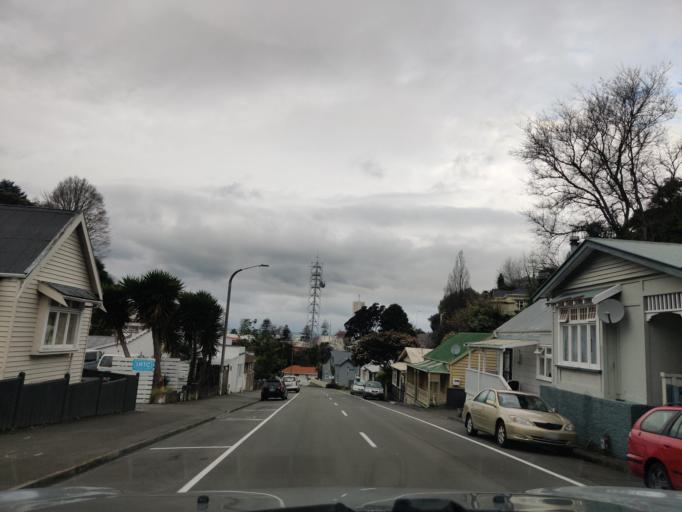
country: NZ
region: Hawke's Bay
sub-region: Napier City
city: Napier
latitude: -39.4875
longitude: 176.9143
